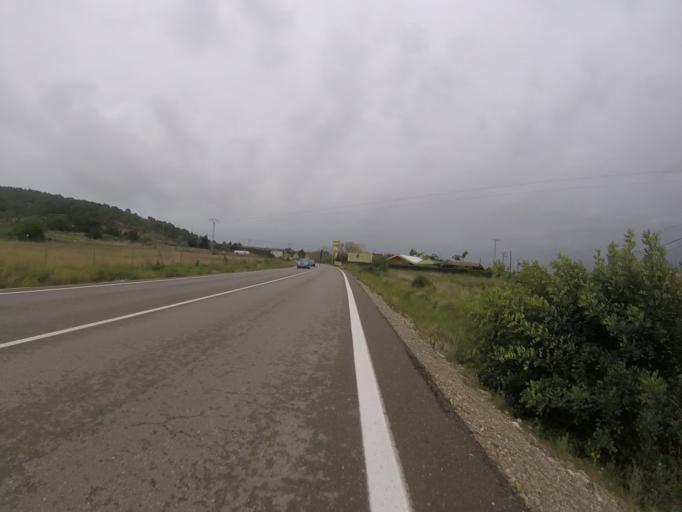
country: ES
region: Valencia
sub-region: Provincia de Castello
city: Alcoceber
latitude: 40.2534
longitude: 0.2459
